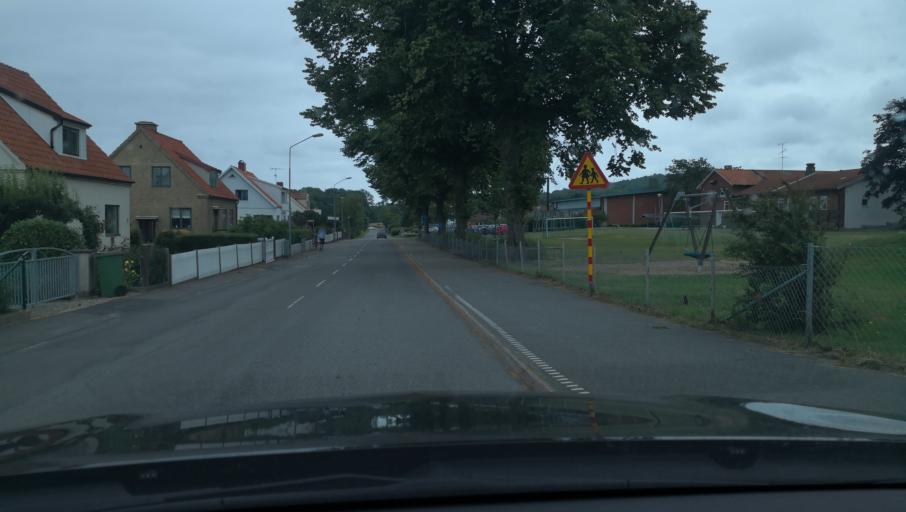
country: SE
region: Skane
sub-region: Simrishamns Kommun
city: Kivik
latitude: 55.6848
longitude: 14.2272
